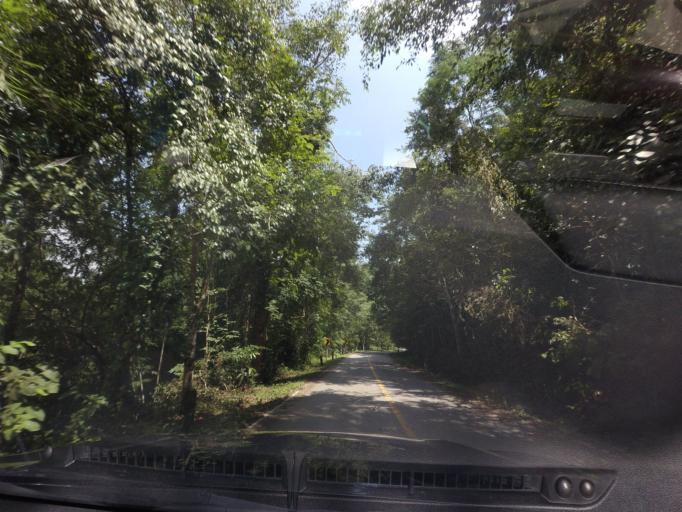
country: TH
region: Loei
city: Na Haeo
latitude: 17.6333
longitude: 100.9039
